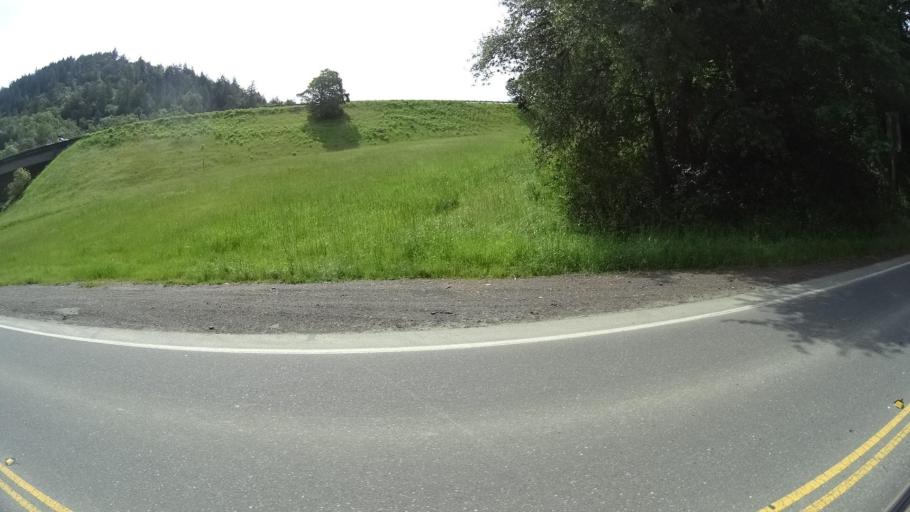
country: US
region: California
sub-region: Humboldt County
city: Redway
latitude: 40.1411
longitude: -123.8099
